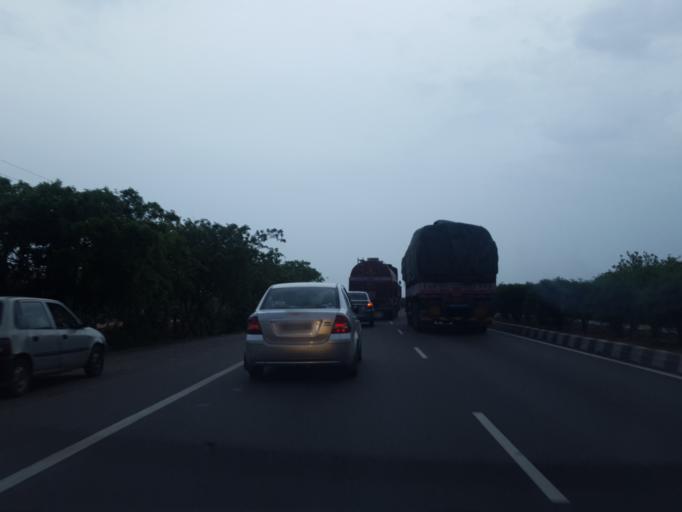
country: IN
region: Telangana
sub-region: Mahbubnagar
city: Farrukhnagar
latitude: 17.1026
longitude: 78.2534
